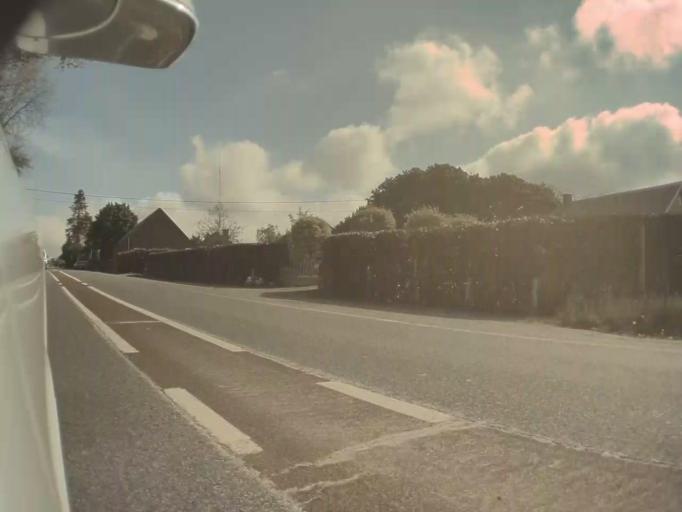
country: BE
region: Wallonia
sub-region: Province de Namur
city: Somme-Leuze
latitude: 50.3408
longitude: 5.3702
